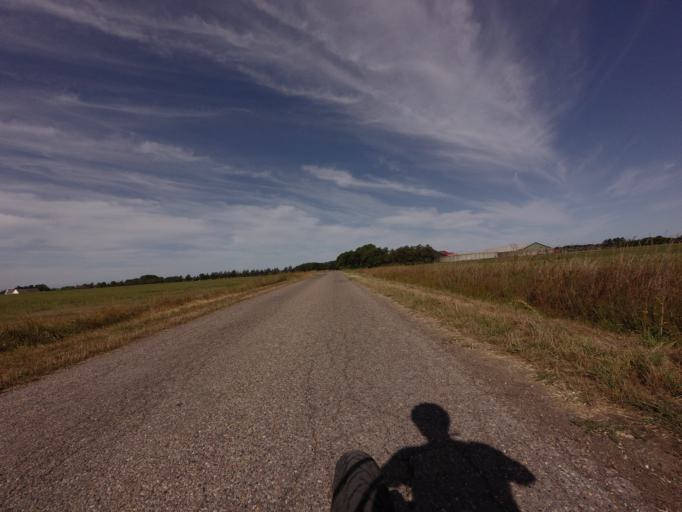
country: DK
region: North Denmark
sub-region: Hjorring Kommune
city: Vra
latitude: 57.3993
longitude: 9.9537
